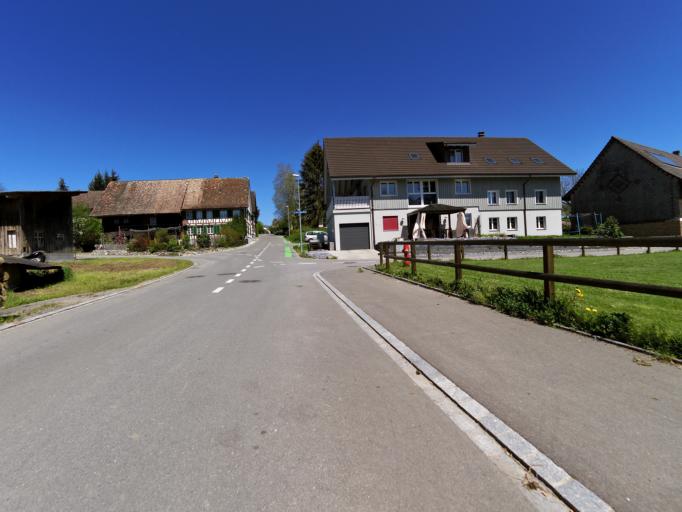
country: CH
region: Thurgau
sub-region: Weinfelden District
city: Berg
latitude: 47.6099
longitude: 9.1539
